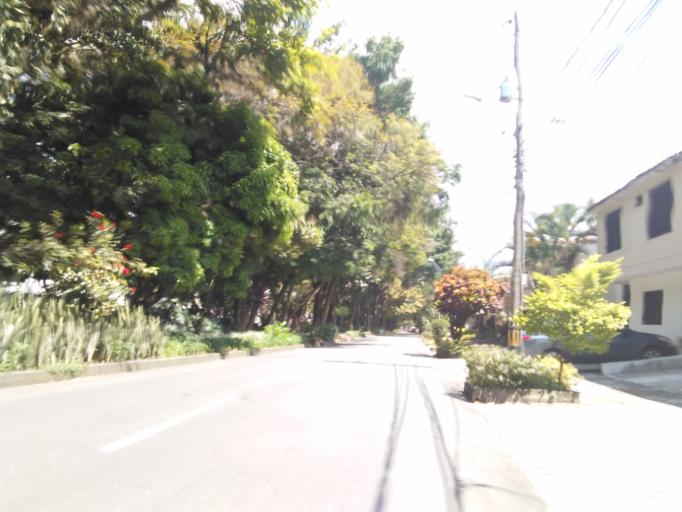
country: CO
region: Antioquia
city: Medellin
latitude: 6.2383
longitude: -75.5935
